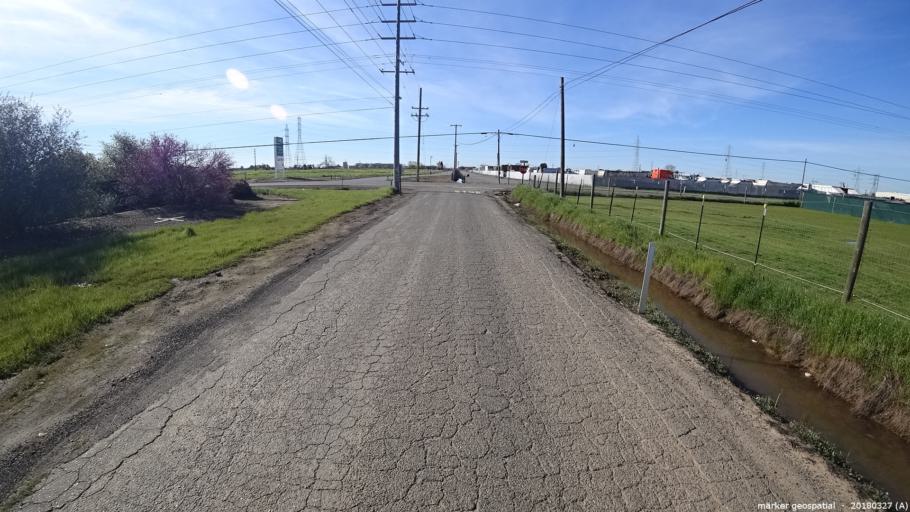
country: US
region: California
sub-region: Sacramento County
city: Rosemont
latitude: 38.5112
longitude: -121.3442
